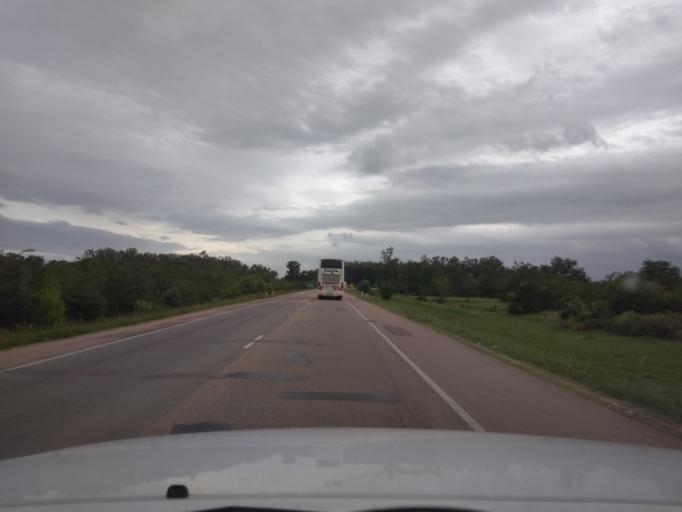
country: UY
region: Canelones
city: Canelones
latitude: -34.5168
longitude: -56.2737
